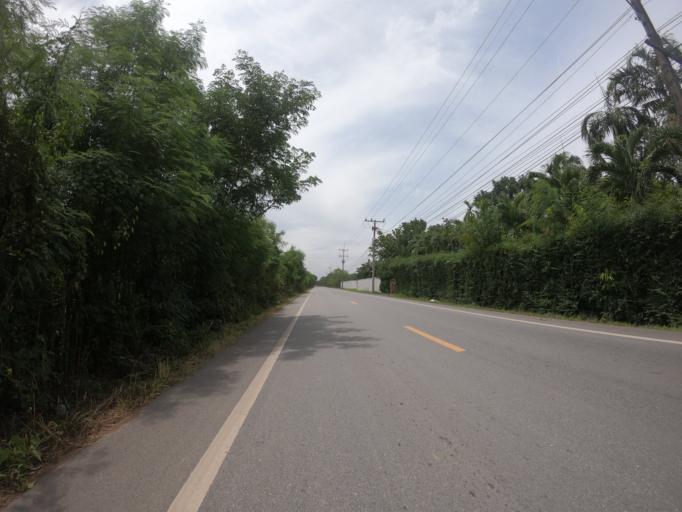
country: TH
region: Pathum Thani
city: Nong Suea
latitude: 14.0619
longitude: 100.8715
